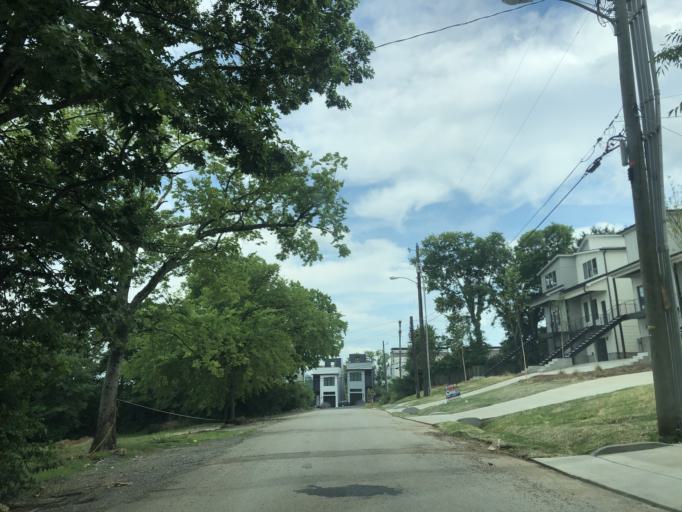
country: US
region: Tennessee
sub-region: Davidson County
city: Nashville
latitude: 36.1963
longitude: -86.7733
